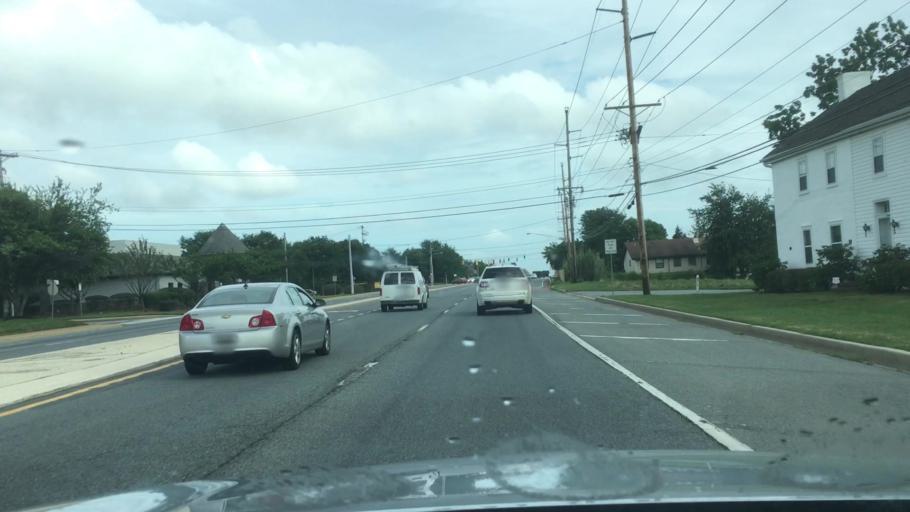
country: US
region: Delaware
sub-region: New Castle County
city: Pike Creek Valley
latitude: 39.7431
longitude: -75.6946
